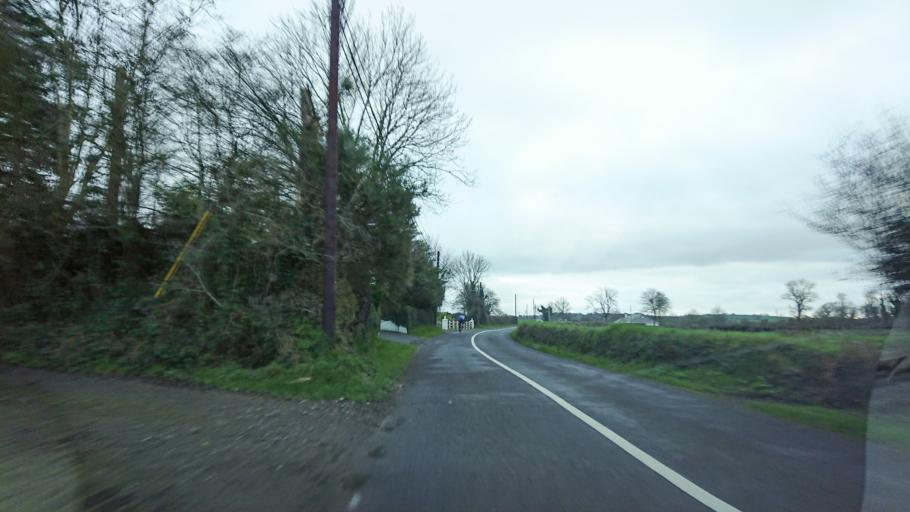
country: IE
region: Munster
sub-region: Waterford
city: Portlaw
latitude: 52.1854
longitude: -7.4086
